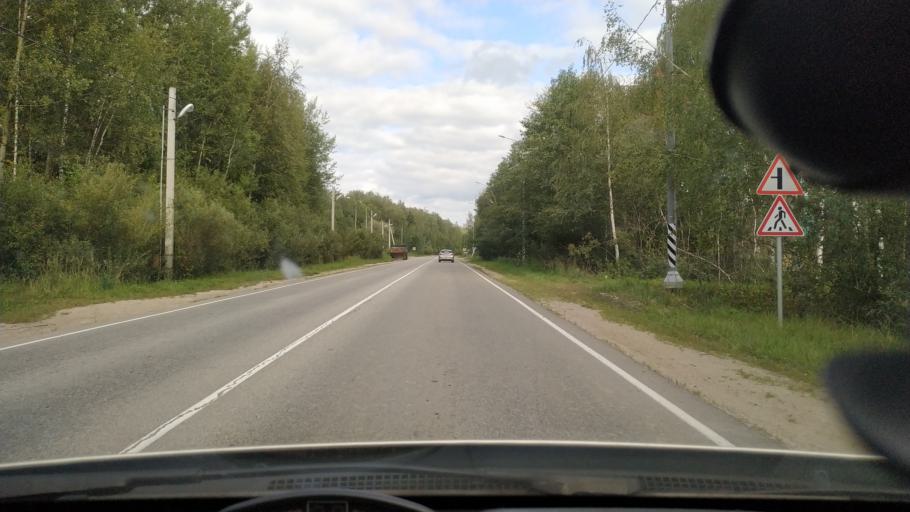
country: RU
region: Moskovskaya
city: Likino-Dulevo
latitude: 55.7294
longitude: 39.0106
